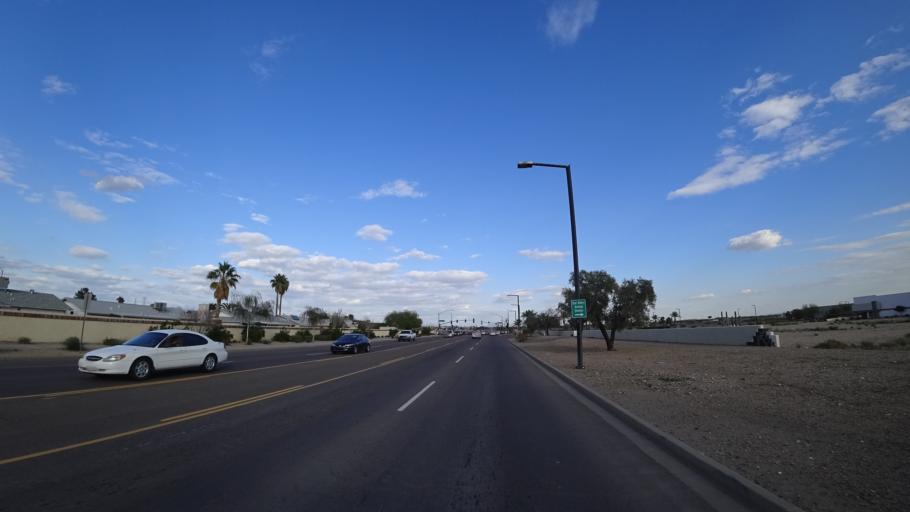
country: US
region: Arizona
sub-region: Maricopa County
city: Youngtown
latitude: 33.5511
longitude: -112.2830
